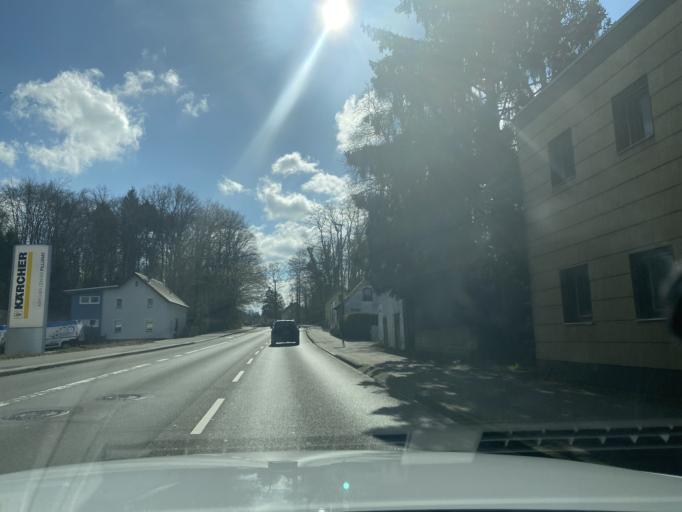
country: DE
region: North Rhine-Westphalia
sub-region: Regierungsbezirk Koln
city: Bergisch Gladbach
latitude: 50.9744
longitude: 7.1421
